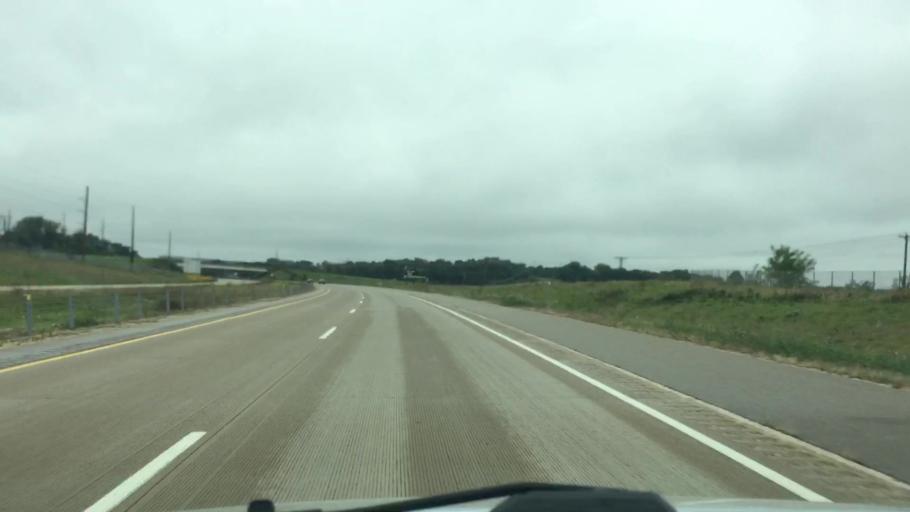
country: US
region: Wisconsin
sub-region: Rock County
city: Milton
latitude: 42.7609
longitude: -88.9387
